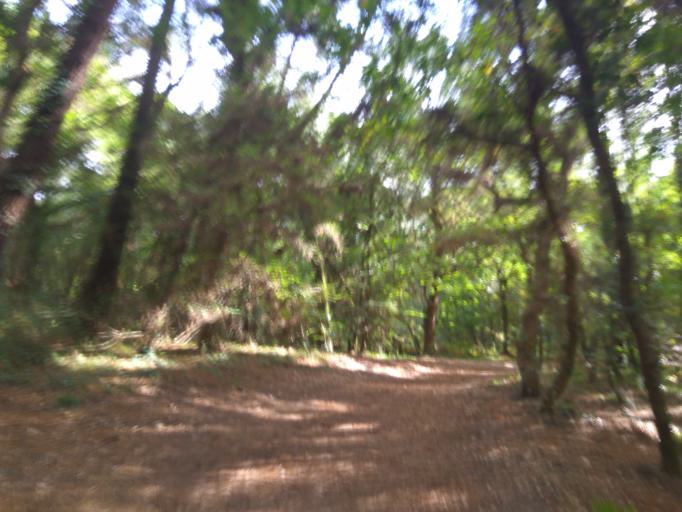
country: FR
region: Aquitaine
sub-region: Departement des Landes
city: Capbreton
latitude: 43.6324
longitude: -1.4425
